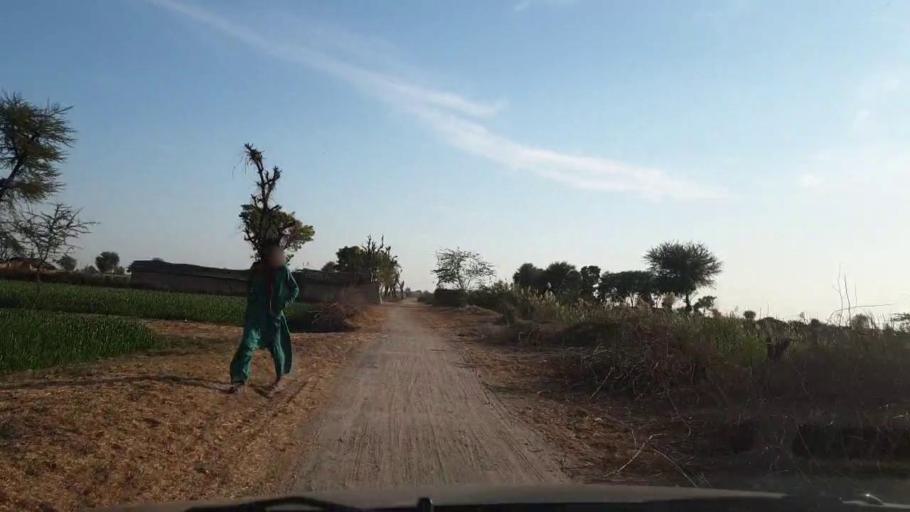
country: PK
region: Sindh
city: Khadro
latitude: 26.2218
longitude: 68.7402
